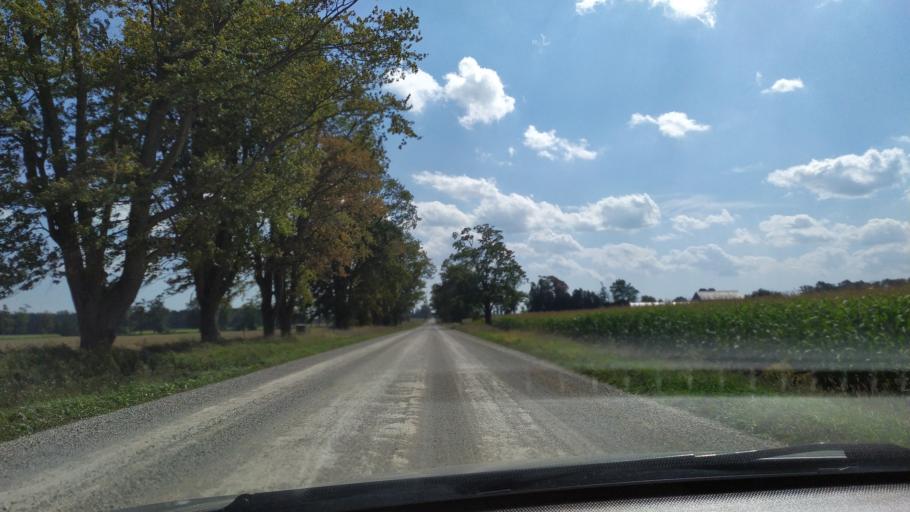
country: CA
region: Ontario
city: Stratford
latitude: 43.2841
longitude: -80.9283
